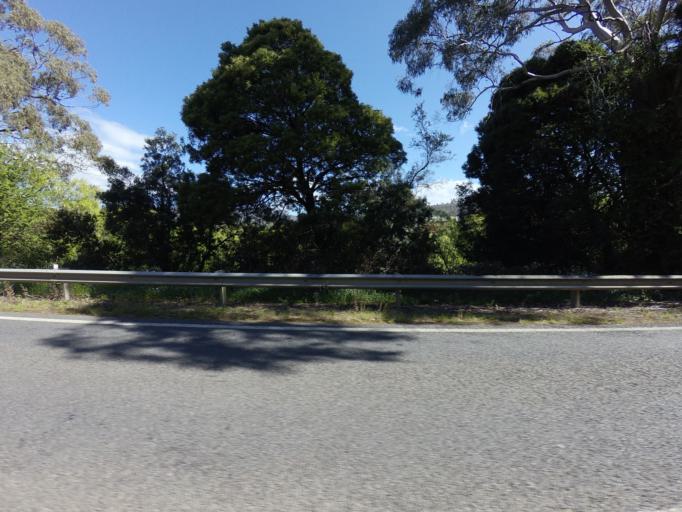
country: AU
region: Tasmania
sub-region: Derwent Valley
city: New Norfolk
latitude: -42.7667
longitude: 147.0237
